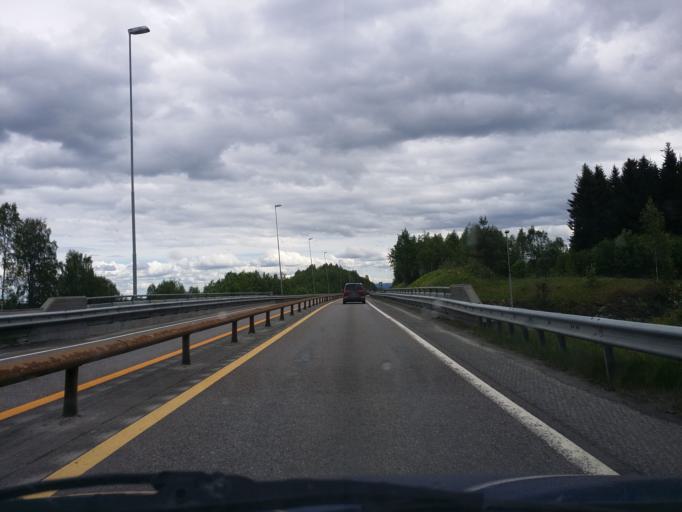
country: NO
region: Hedmark
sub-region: Hamar
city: Hamar
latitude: 60.8477
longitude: 11.0275
